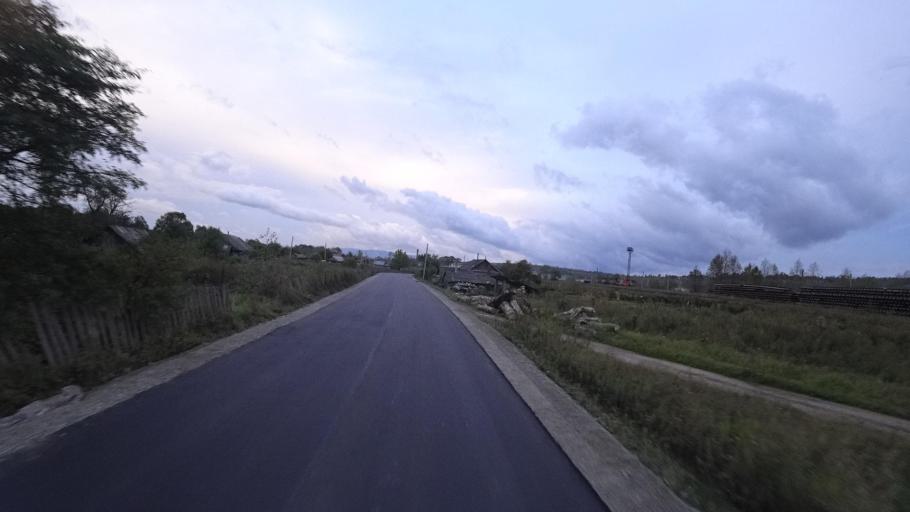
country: RU
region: Jewish Autonomous Oblast
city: Izvestkovyy
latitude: 48.9907
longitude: 131.5457
